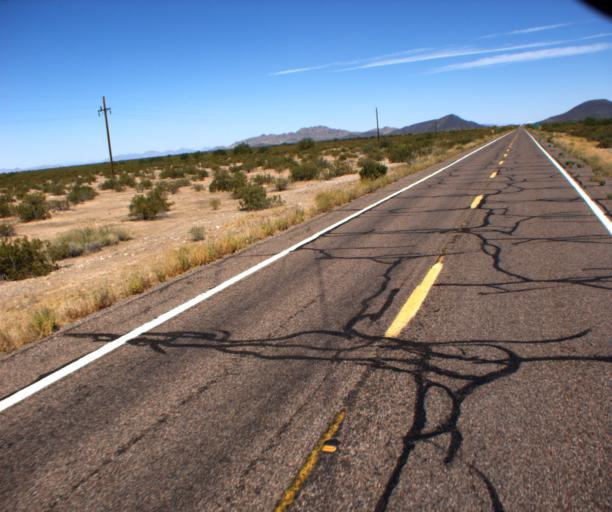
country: US
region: Arizona
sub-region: Maricopa County
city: Gila Bend
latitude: 32.6959
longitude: -112.8507
